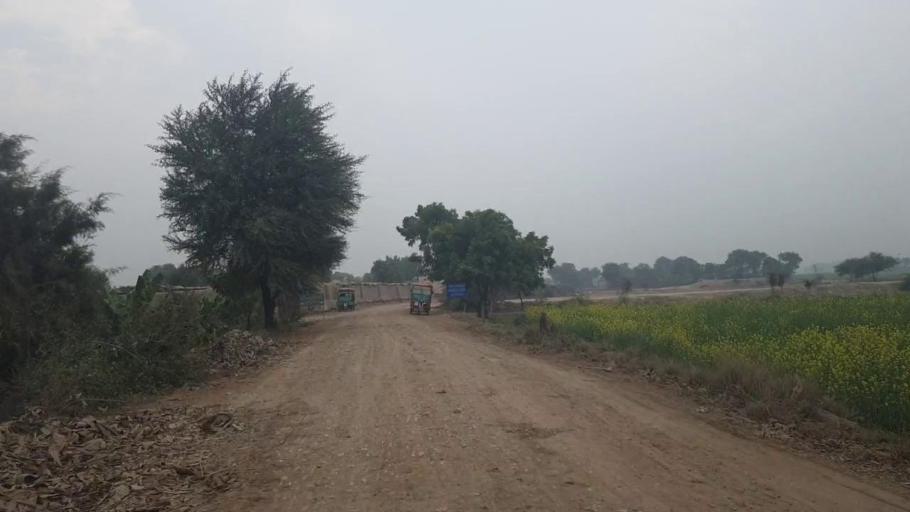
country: PK
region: Sindh
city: Tando Adam
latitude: 25.7051
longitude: 68.6185
